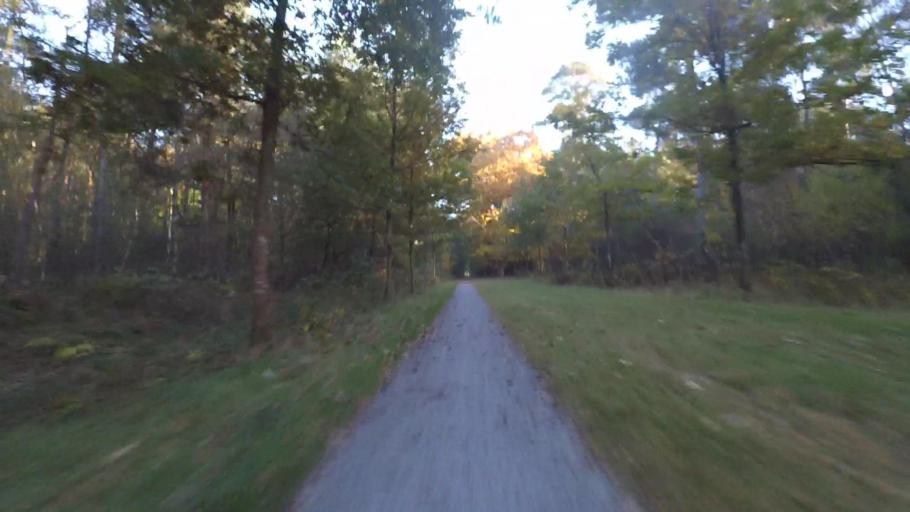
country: NL
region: Utrecht
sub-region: Gemeente De Bilt
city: De Bilt
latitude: 52.1509
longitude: 5.2135
